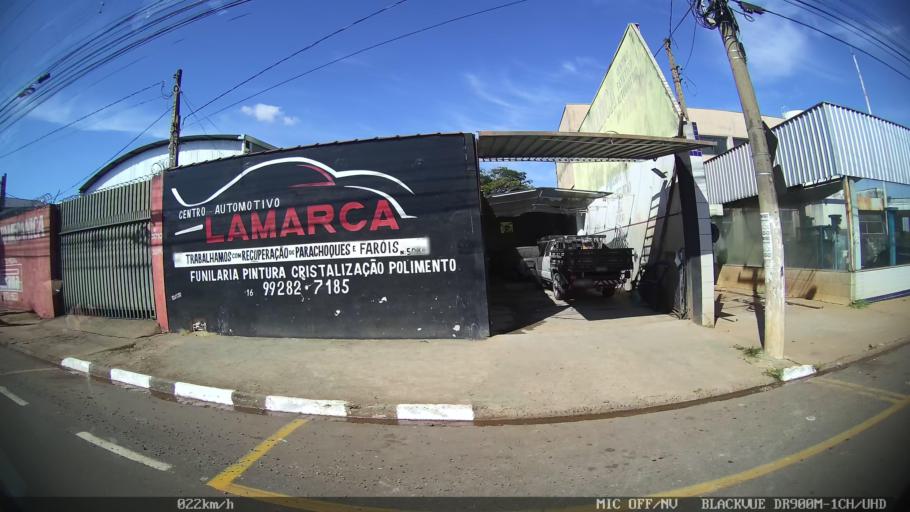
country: BR
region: Sao Paulo
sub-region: Franca
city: Franca
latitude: -20.5096
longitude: -47.3998
